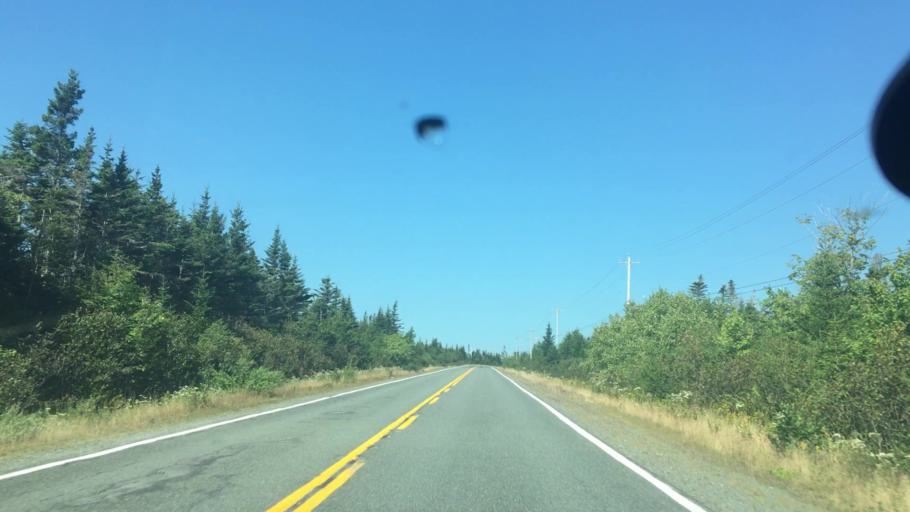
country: CA
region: Nova Scotia
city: Antigonish
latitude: 44.9822
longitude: -62.0932
